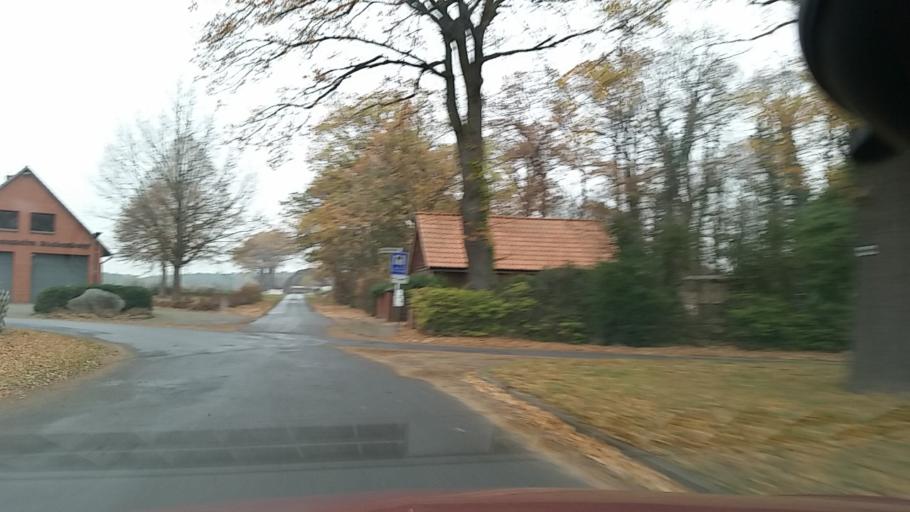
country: DE
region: Lower Saxony
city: Wrestedt
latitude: 52.9128
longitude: 10.5957
